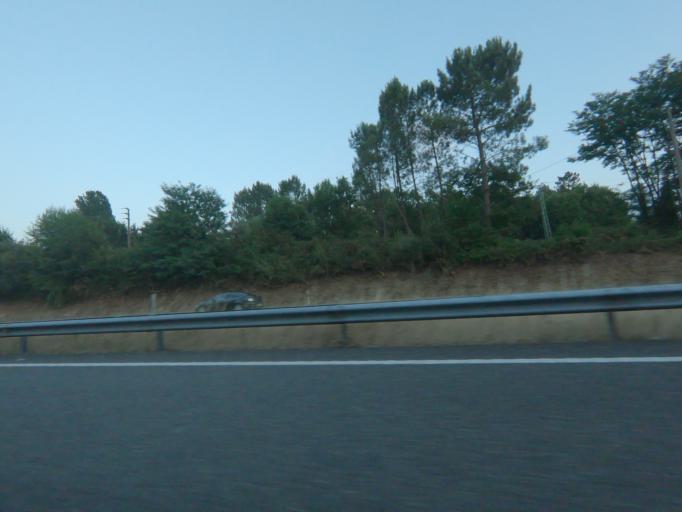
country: ES
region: Galicia
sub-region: Provincia de Pontevedra
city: Ponteareas
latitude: 42.1538
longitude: -8.5105
